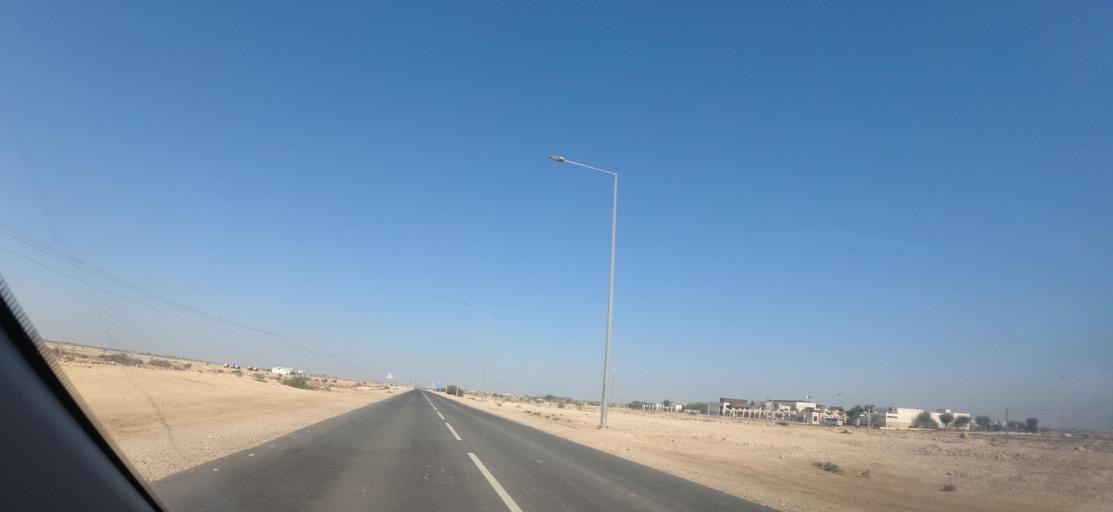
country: QA
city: Al Ghuwayriyah
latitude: 25.8441
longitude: 51.2645
